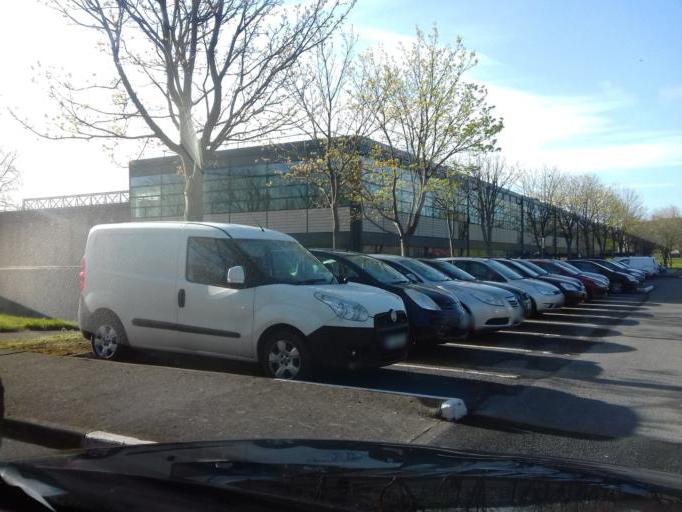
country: IE
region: Leinster
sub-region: Dublin City
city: Finglas
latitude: 53.4006
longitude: -6.2892
